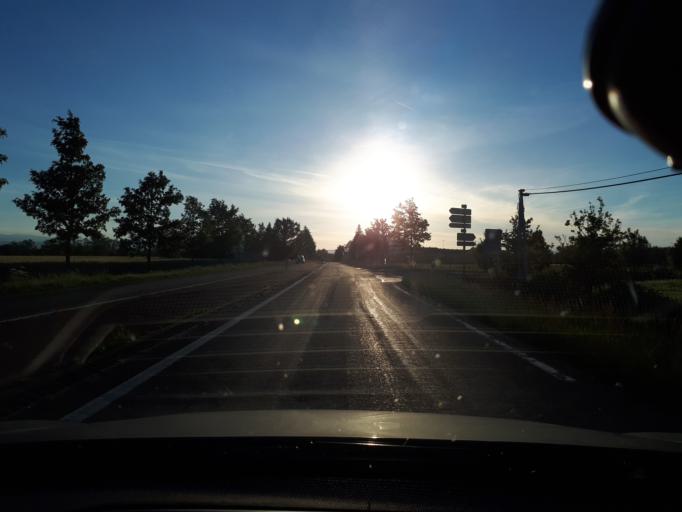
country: FR
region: Rhone-Alpes
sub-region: Departement de la Loire
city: Feurs
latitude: 45.7382
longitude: 4.2625
